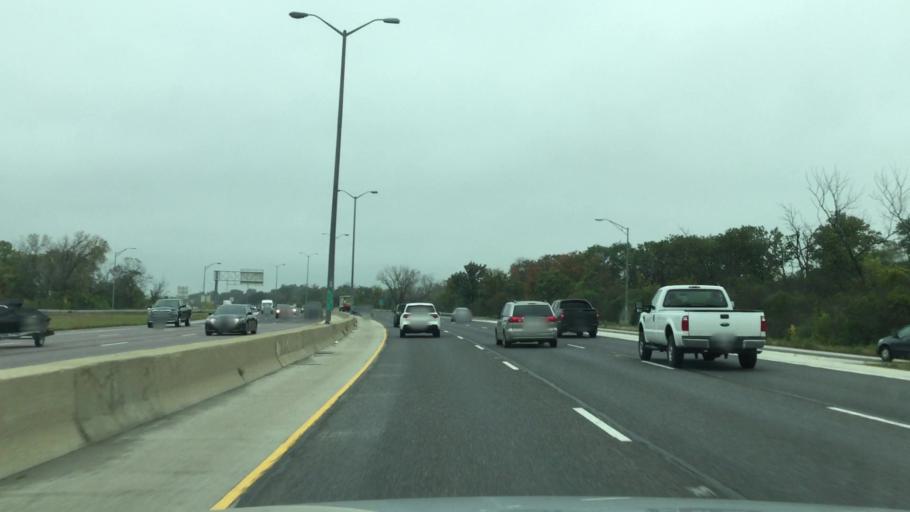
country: US
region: Illinois
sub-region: Cook County
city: Northfield
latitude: 42.0864
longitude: -87.7586
